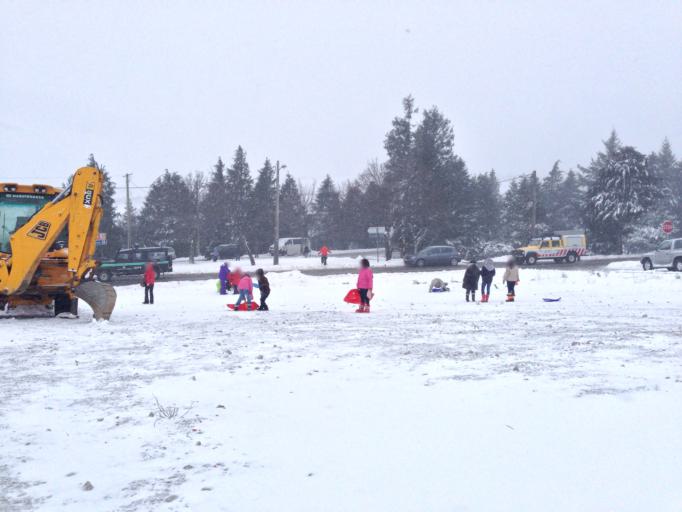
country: PT
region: Castelo Branco
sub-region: Covilha
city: Covilha
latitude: 40.3090
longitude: -7.5497
